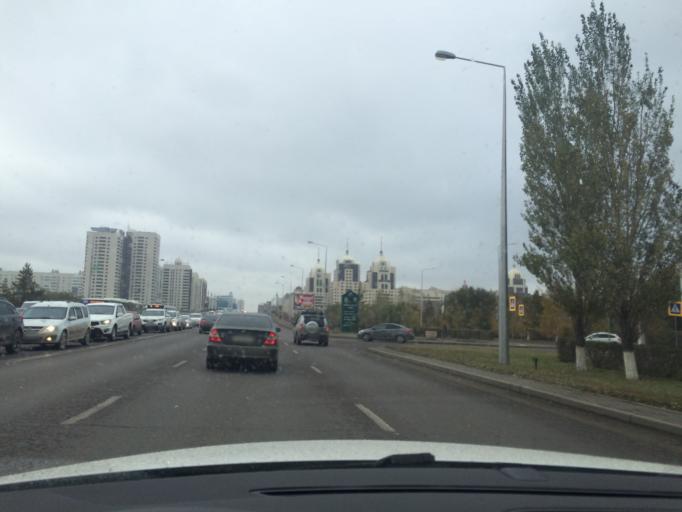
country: KZ
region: Astana Qalasy
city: Astana
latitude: 51.1541
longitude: 71.4125
